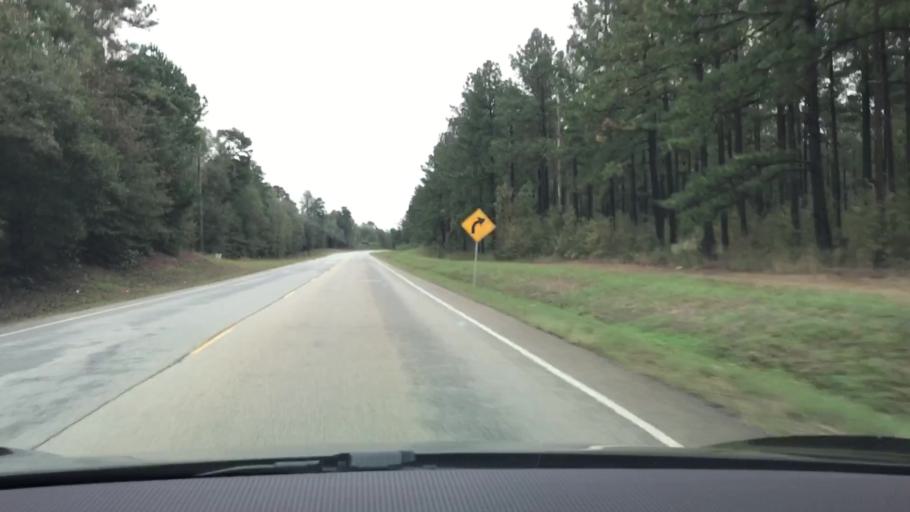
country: US
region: Georgia
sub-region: Jefferson County
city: Louisville
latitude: 33.0919
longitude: -82.4169
